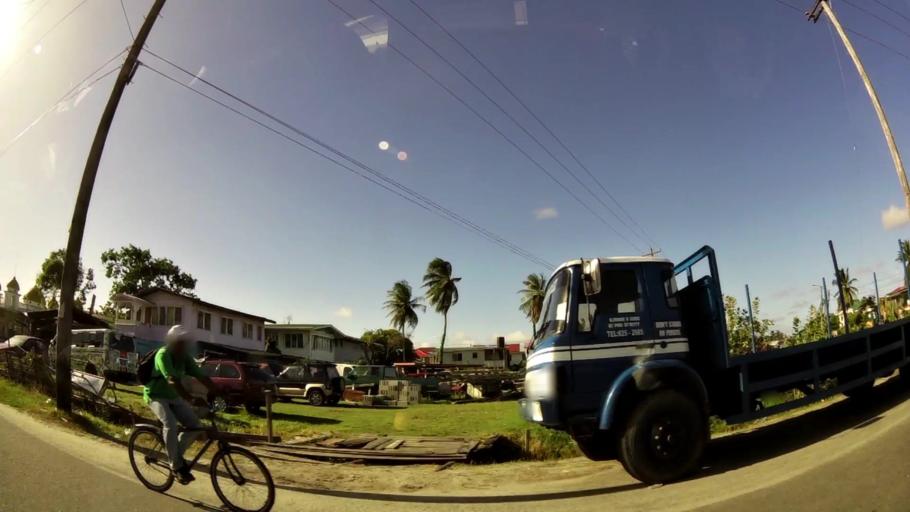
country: GY
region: Demerara-Mahaica
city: Georgetown
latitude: 6.8168
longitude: -58.1397
